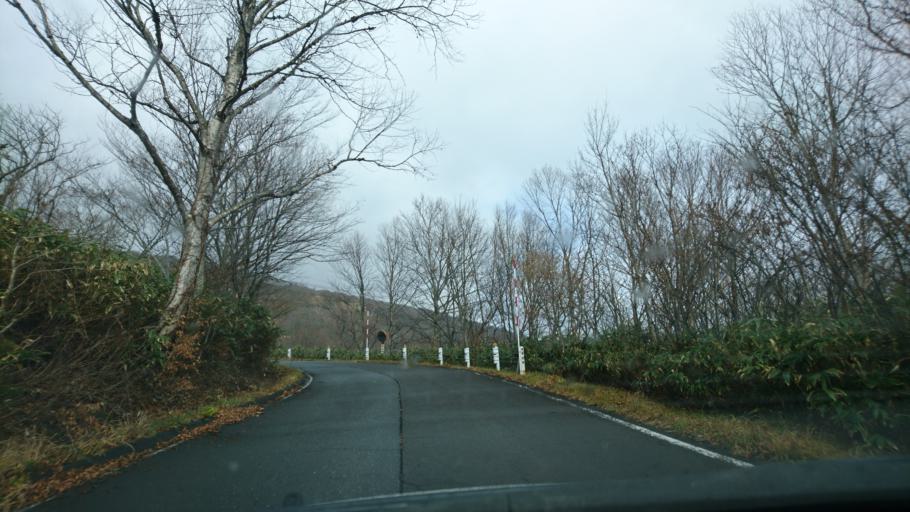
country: JP
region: Iwate
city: Ichinoseki
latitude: 38.9391
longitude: 140.8276
